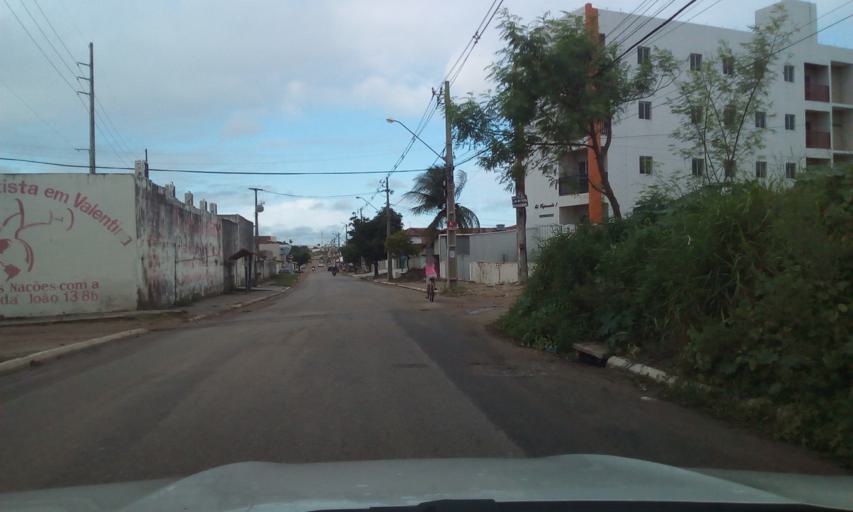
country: BR
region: Paraiba
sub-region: Conde
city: Conde
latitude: -7.2072
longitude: -34.8531
